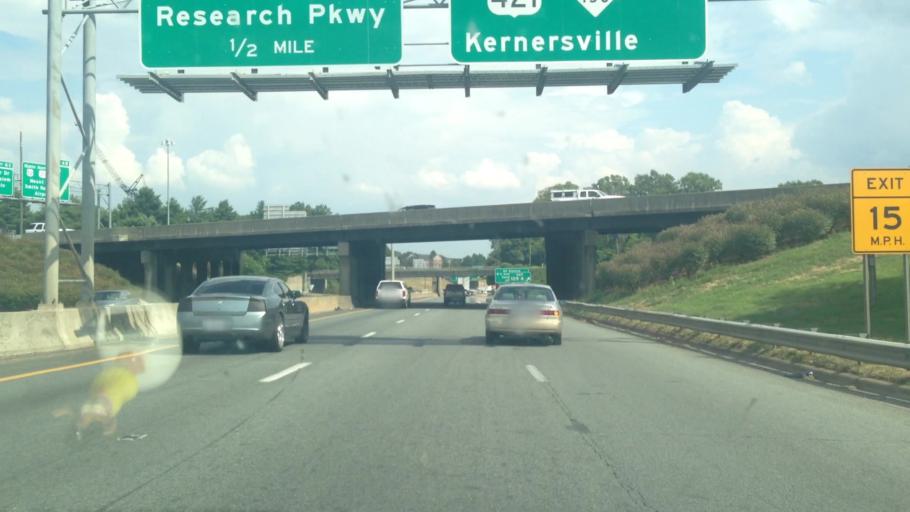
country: US
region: North Carolina
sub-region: Forsyth County
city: Winston-Salem
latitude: 36.0946
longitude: -80.2333
